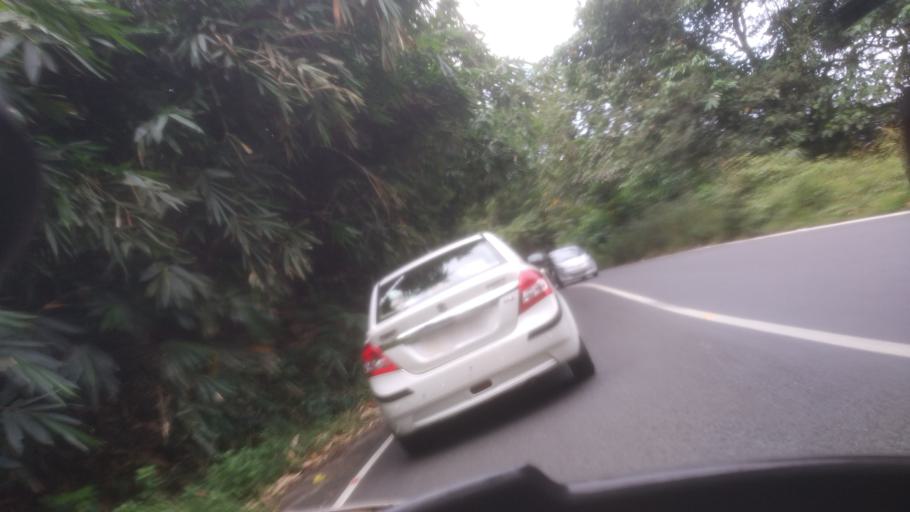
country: IN
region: Kerala
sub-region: Idukki
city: Kuttampuzha
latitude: 10.0618
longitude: 76.8020
